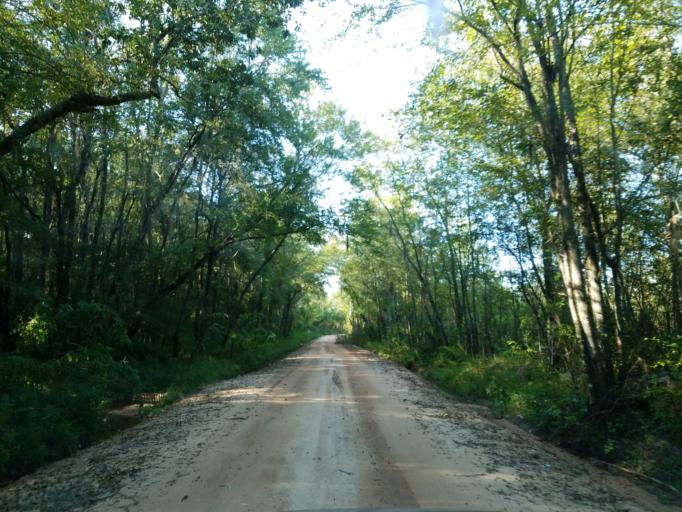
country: US
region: Georgia
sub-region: Lowndes County
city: Hahira
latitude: 31.0319
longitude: -83.3934
